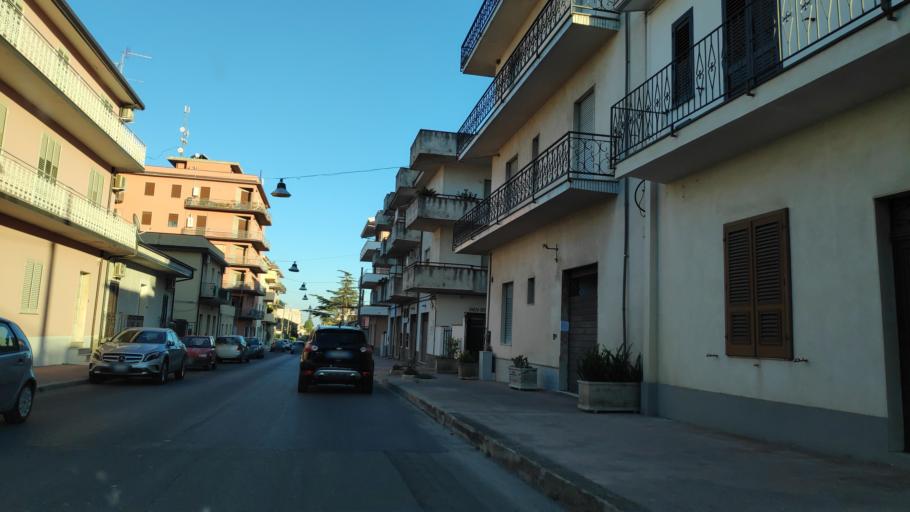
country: IT
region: Calabria
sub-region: Provincia di Reggio Calabria
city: Locri
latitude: 38.2388
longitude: 16.2555
